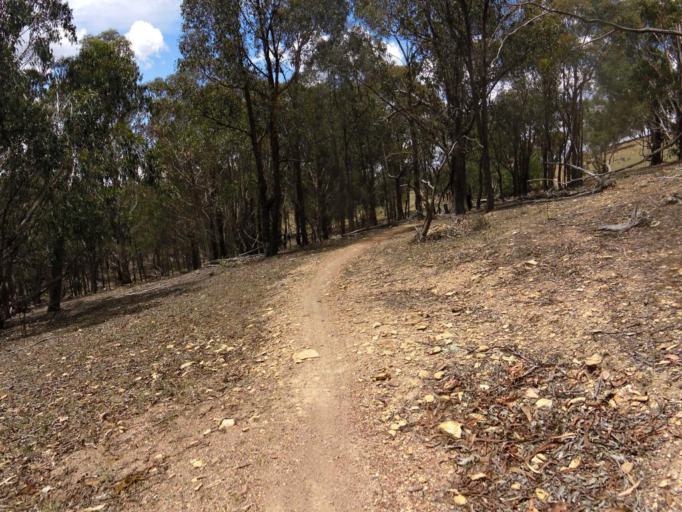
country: AU
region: Australian Capital Territory
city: Kaleen
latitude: -35.1345
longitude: 149.1369
